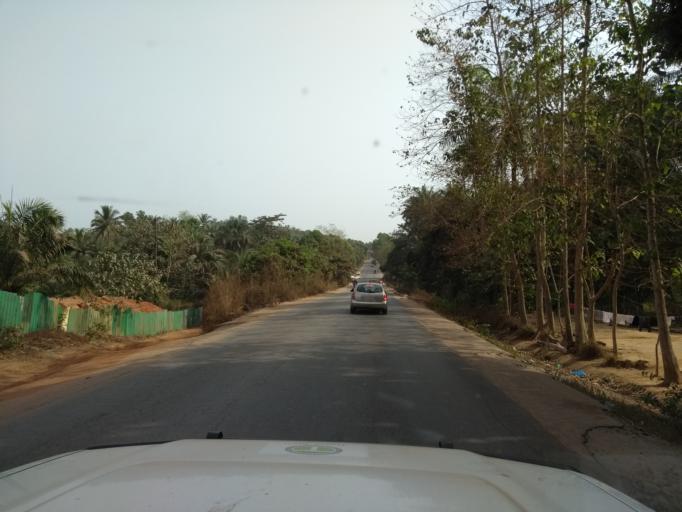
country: GN
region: Kindia
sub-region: Prefecture de Dubreka
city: Dubreka
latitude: 9.8417
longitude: -13.4877
